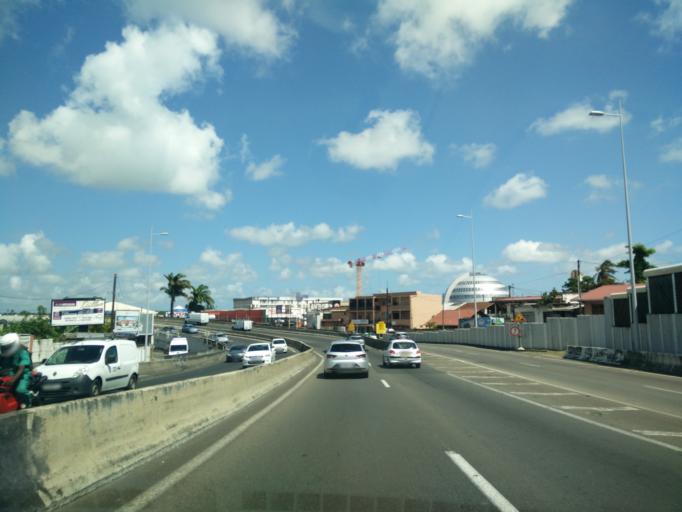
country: MQ
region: Martinique
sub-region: Martinique
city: Fort-de-France
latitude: 14.6148
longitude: -61.0532
